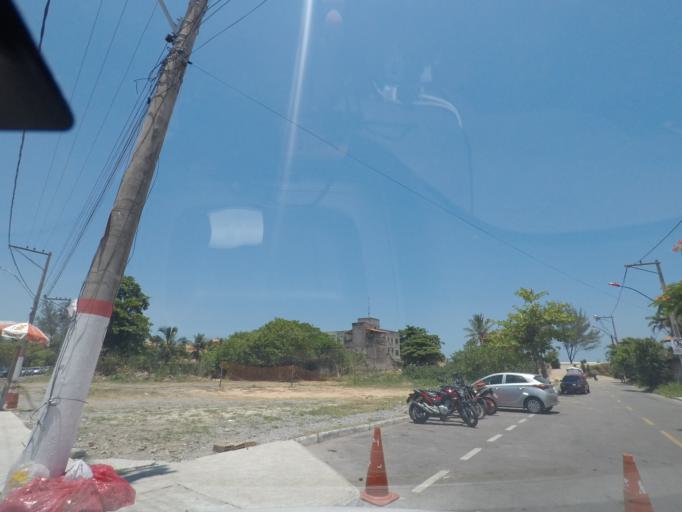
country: BR
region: Rio de Janeiro
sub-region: Niteroi
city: Niteroi
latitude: -22.9696
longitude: -43.0134
